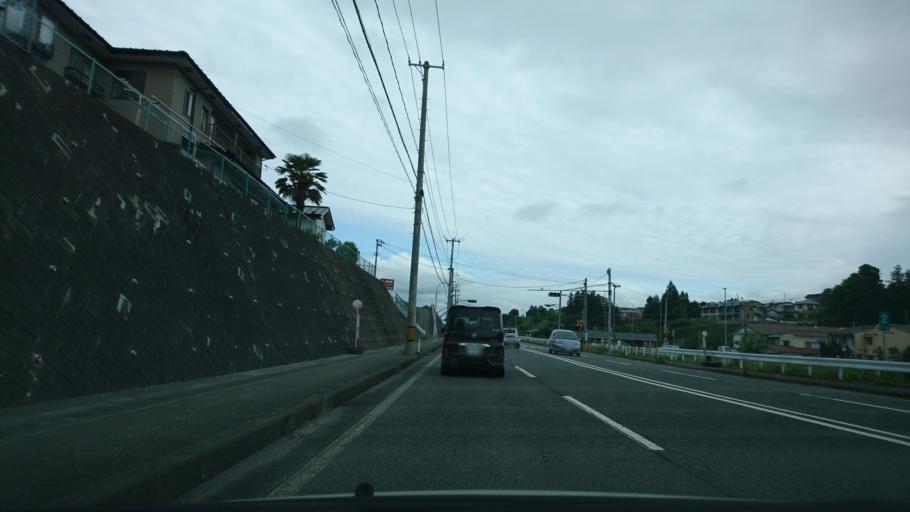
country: JP
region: Iwate
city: Ichinoseki
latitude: 38.9160
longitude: 141.1417
